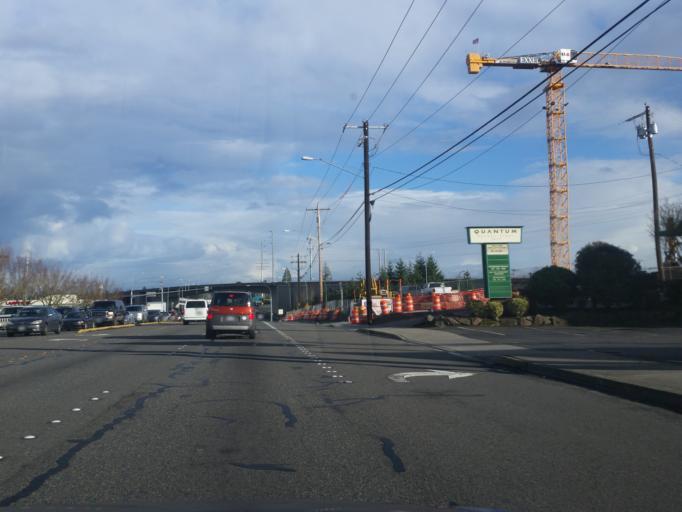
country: US
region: Washington
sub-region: Snohomish County
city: Alderwood Manor
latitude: 47.8209
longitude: -122.2853
